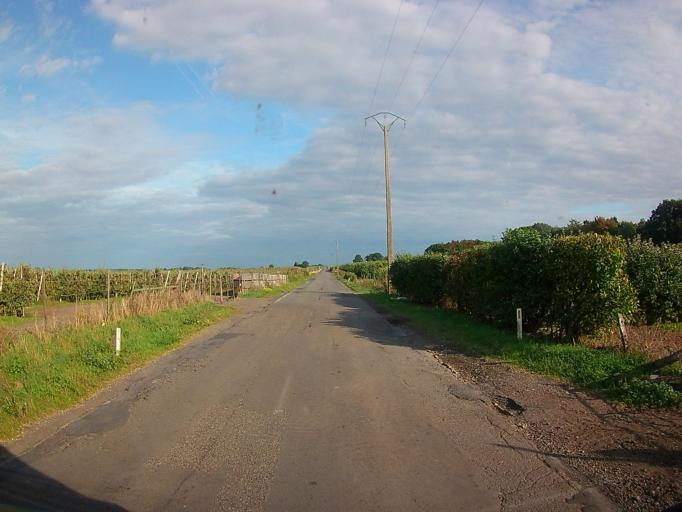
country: BE
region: Flanders
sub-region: Provincie Limburg
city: Sint-Pieters-Voeren
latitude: 50.7183
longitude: 5.8016
